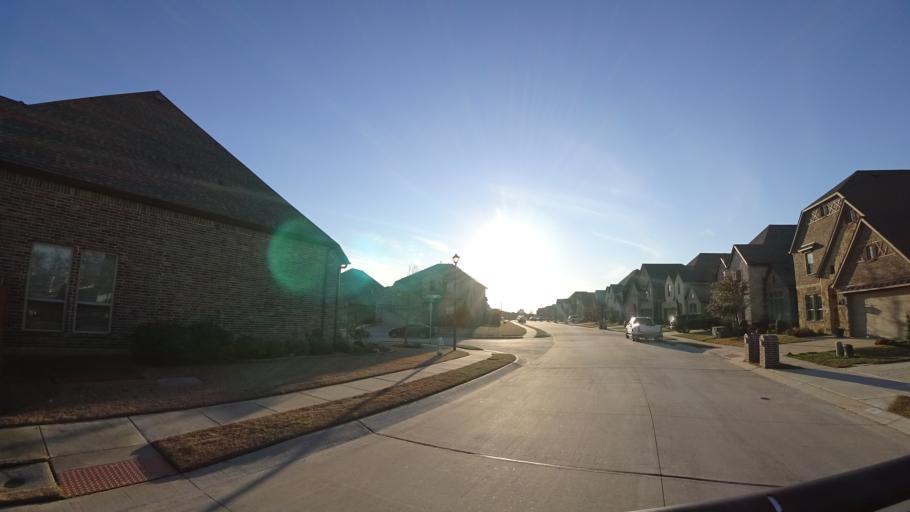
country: US
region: Texas
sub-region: Dallas County
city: Coppell
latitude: 32.9948
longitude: -96.9955
